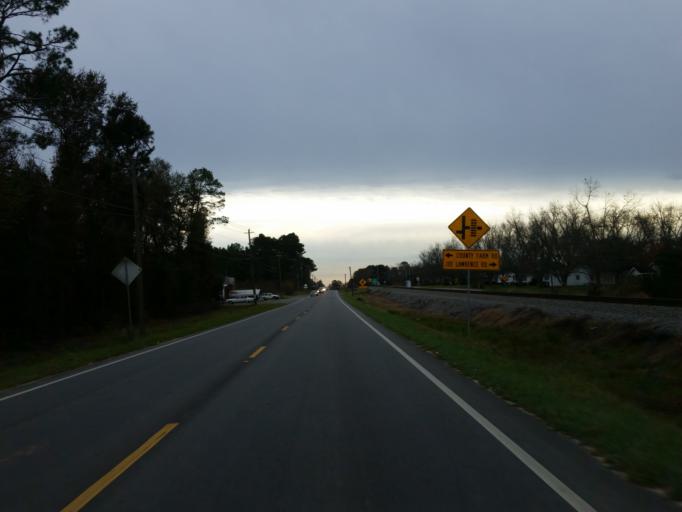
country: US
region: Georgia
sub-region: Turner County
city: Ashburn
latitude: 31.6863
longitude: -83.6436
